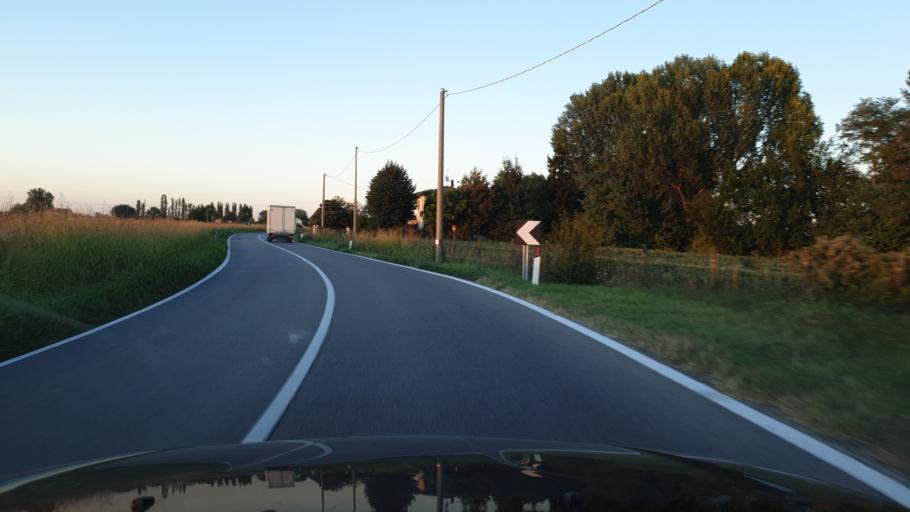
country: IT
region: Emilia-Romagna
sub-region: Provincia di Bologna
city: Progresso
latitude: 44.5671
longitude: 11.4021
